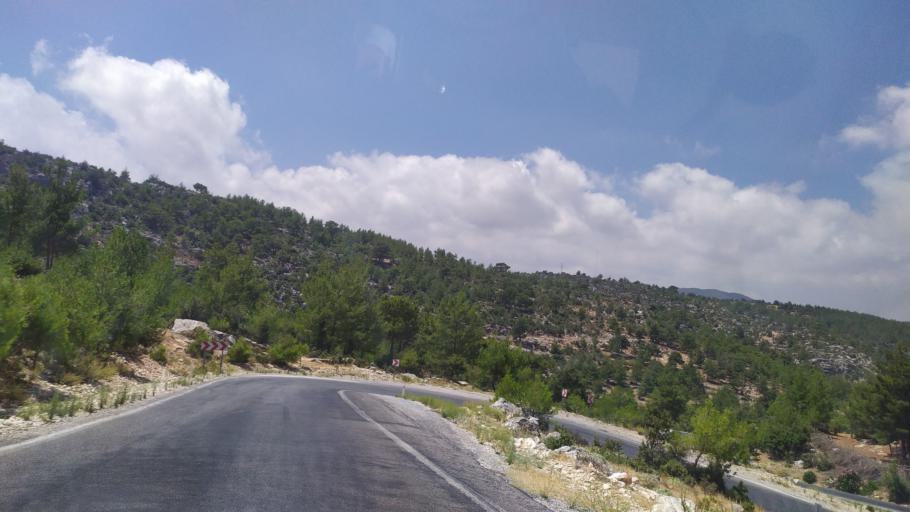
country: TR
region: Mersin
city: Gulnar
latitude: 36.2750
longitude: 33.3856
